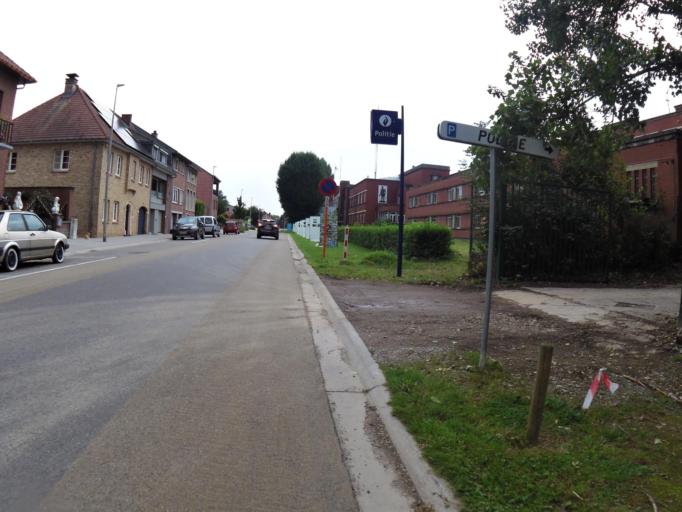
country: BE
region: Flanders
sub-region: Provincie Limburg
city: Tongeren
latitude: 50.7826
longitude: 5.4801
